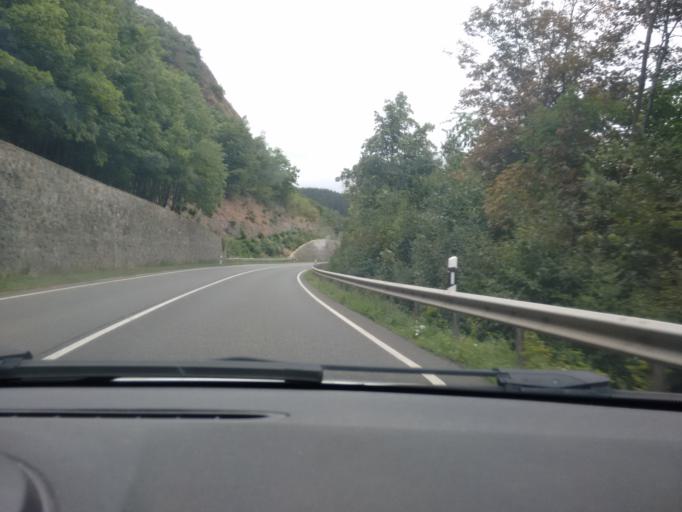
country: DE
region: Rheinland-Pfalz
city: Kirn
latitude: 49.7776
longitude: 7.4550
